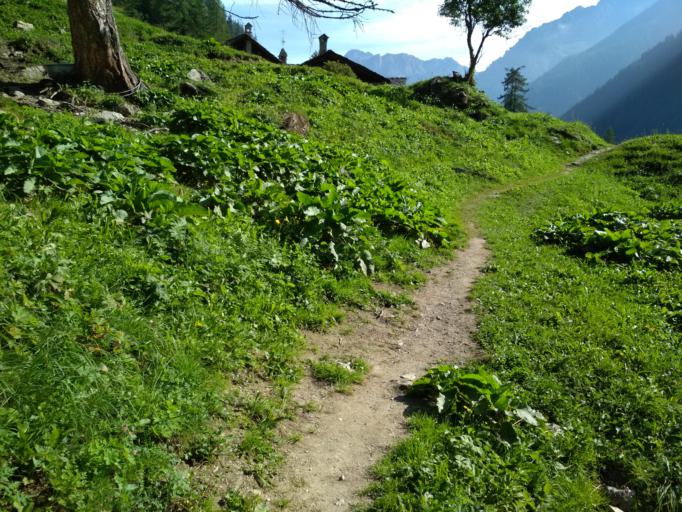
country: IT
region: Aosta Valley
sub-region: Valle d'Aosta
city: Gressoney-Saint-Jean
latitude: 45.8002
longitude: 7.8263
